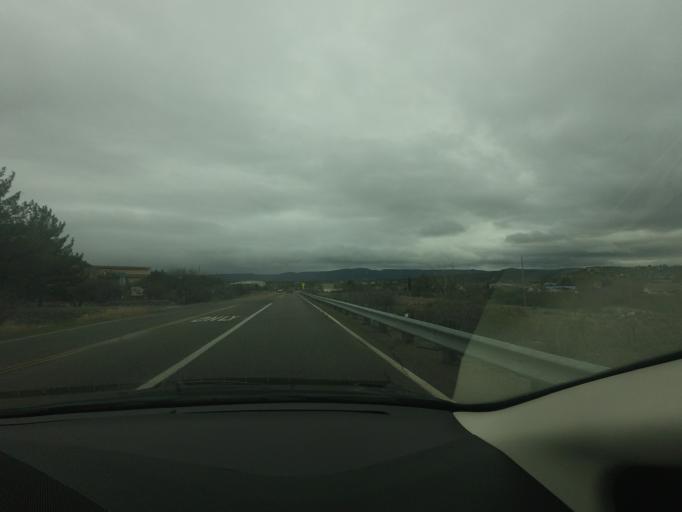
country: US
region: Arizona
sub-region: Yavapai County
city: Lake Montezuma
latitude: 34.6550
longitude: -111.7739
